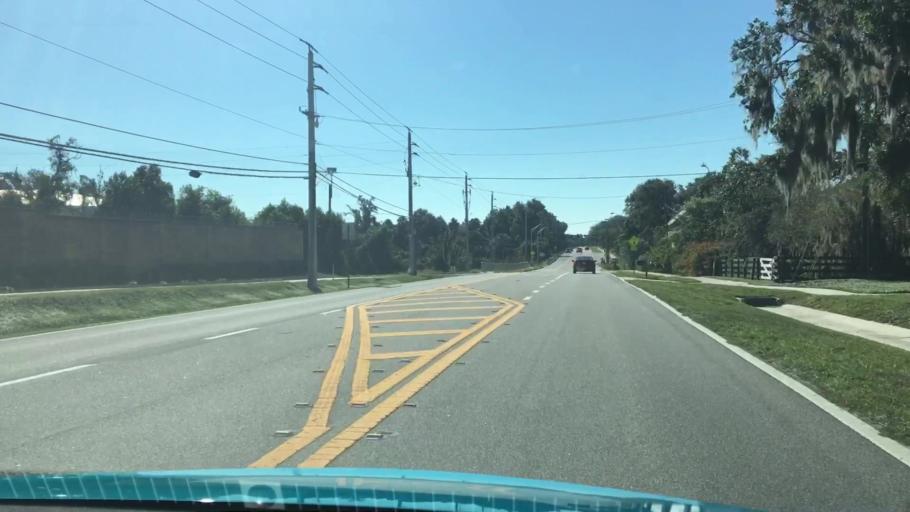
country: US
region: Florida
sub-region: Seminole County
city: Heathrow
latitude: 28.7958
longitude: -81.3630
